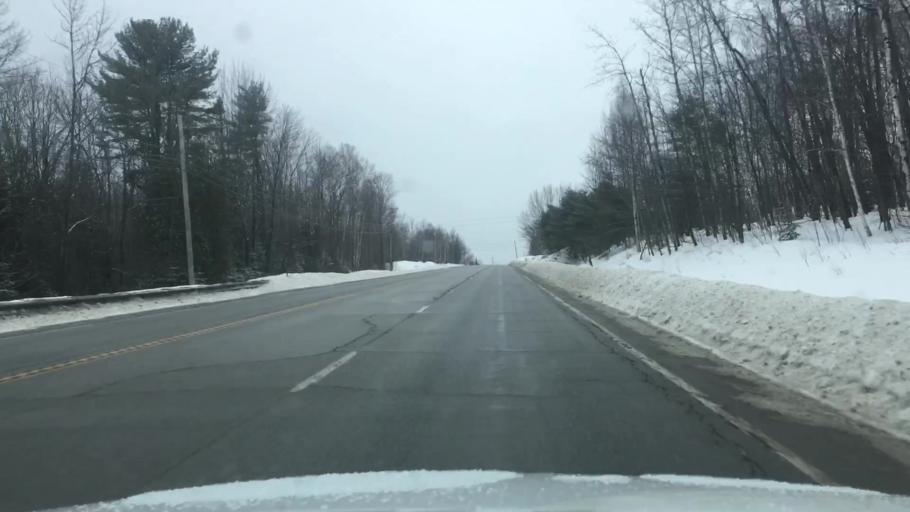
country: US
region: Maine
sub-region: Oxford County
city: Peru
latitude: 44.5794
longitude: -70.3698
